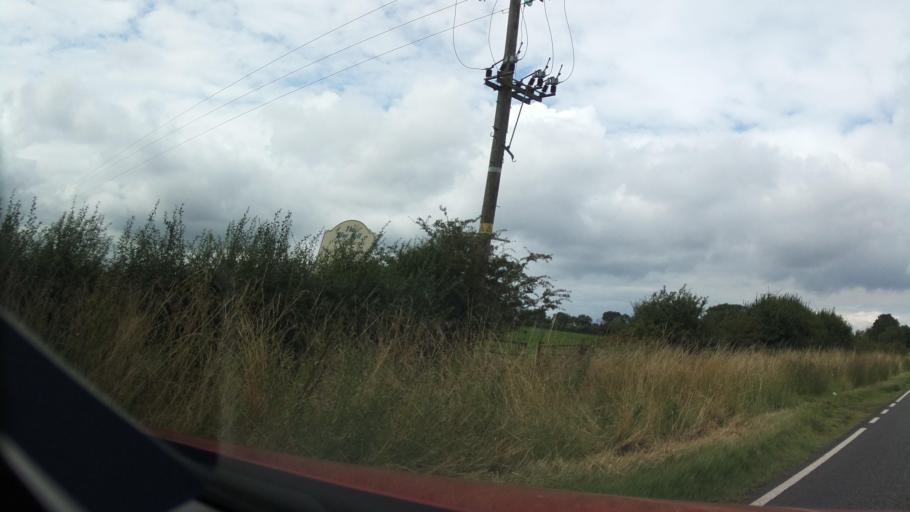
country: GB
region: England
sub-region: District of Rutland
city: Ryhall
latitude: 52.6754
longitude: -0.4703
